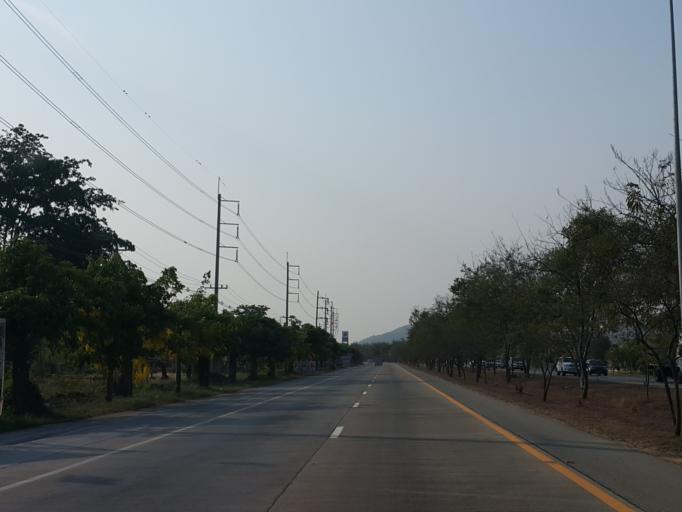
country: TH
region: Suphan Buri
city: Doembang Nangbuat
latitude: 14.8321
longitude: 100.1129
